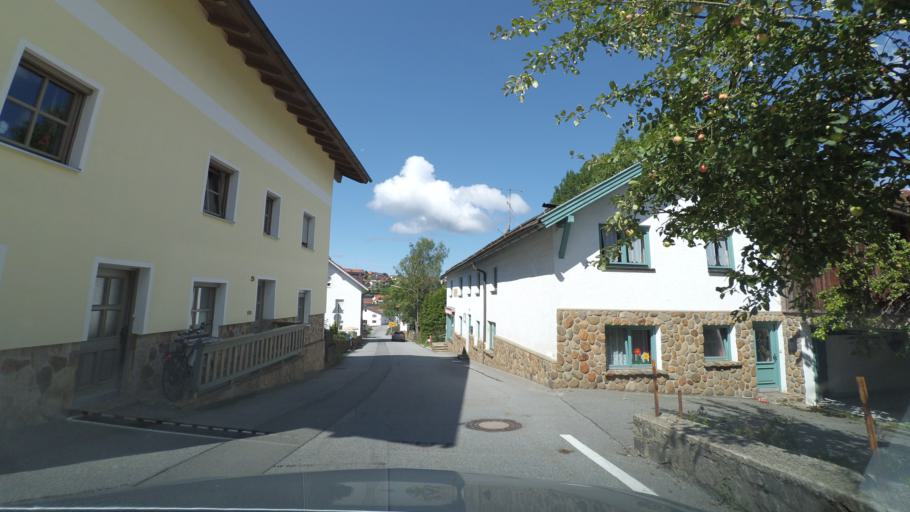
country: DE
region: Bavaria
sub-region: Lower Bavaria
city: Bodenmais
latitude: 49.0676
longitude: 13.1077
